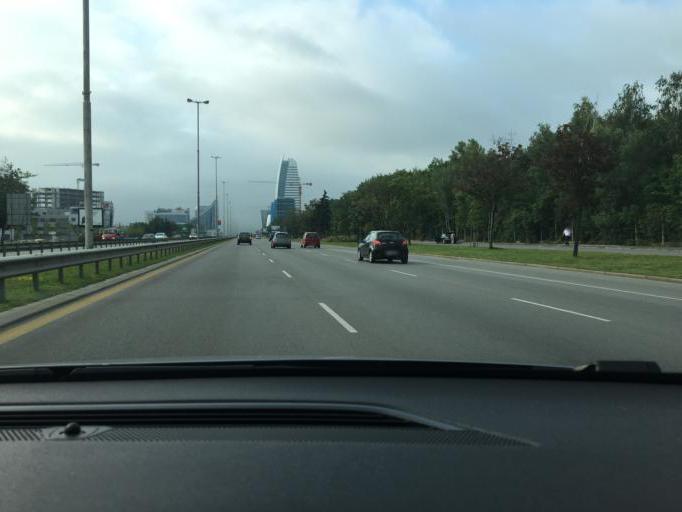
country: BG
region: Sofia-Capital
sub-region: Stolichna Obshtina
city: Sofia
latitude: 42.6535
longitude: 23.3892
